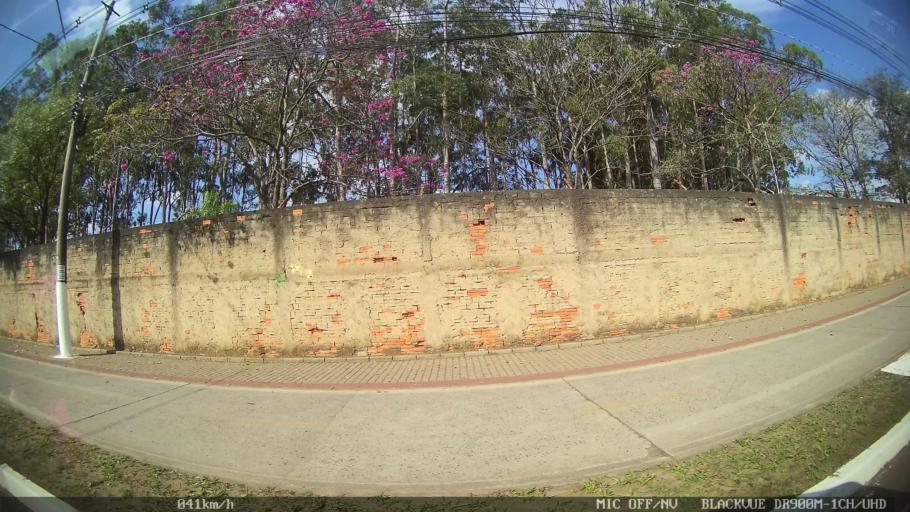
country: BR
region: Sao Paulo
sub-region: Hortolandia
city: Hortolandia
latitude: -22.8798
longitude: -47.2304
